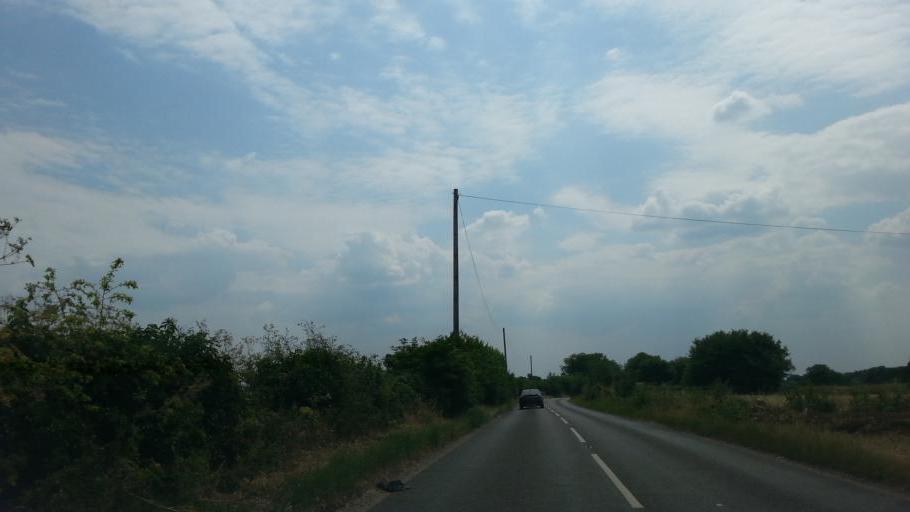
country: GB
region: England
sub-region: Suffolk
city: Lakenheath
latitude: 52.3974
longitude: 0.5296
